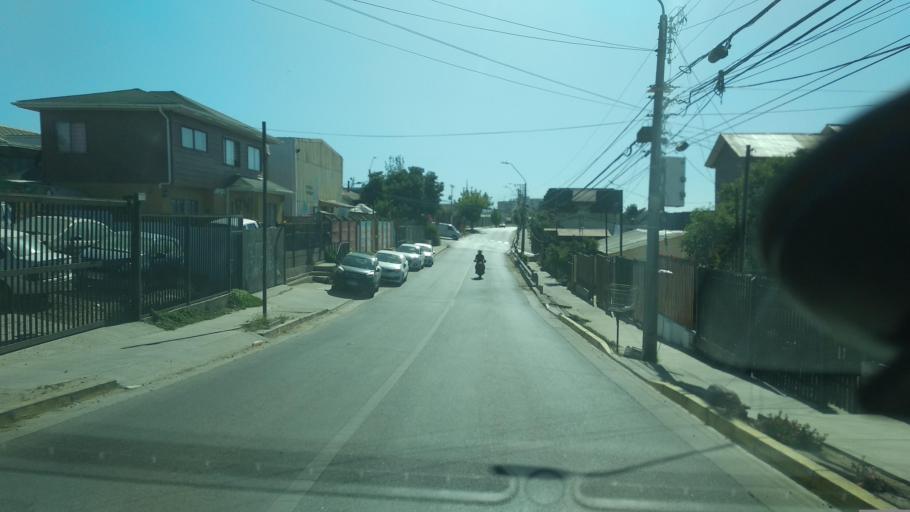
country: CL
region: Valparaiso
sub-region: Provincia de Marga Marga
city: Villa Alemana
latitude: -33.0439
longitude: -71.3889
